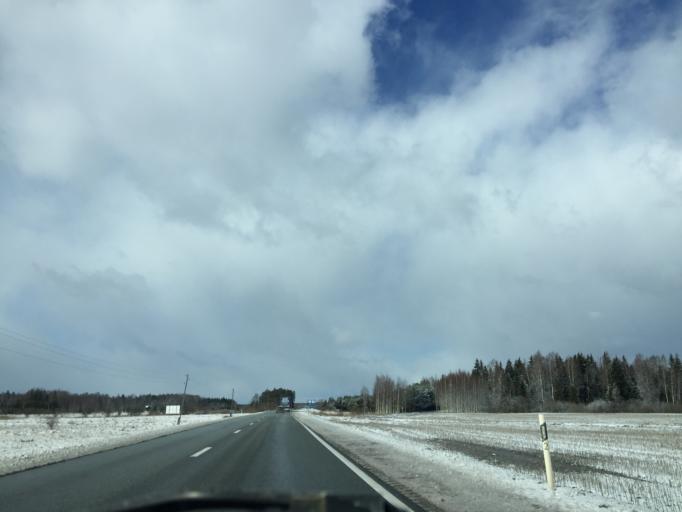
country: LV
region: Kandava
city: Kandava
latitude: 57.0500
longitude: 22.8771
